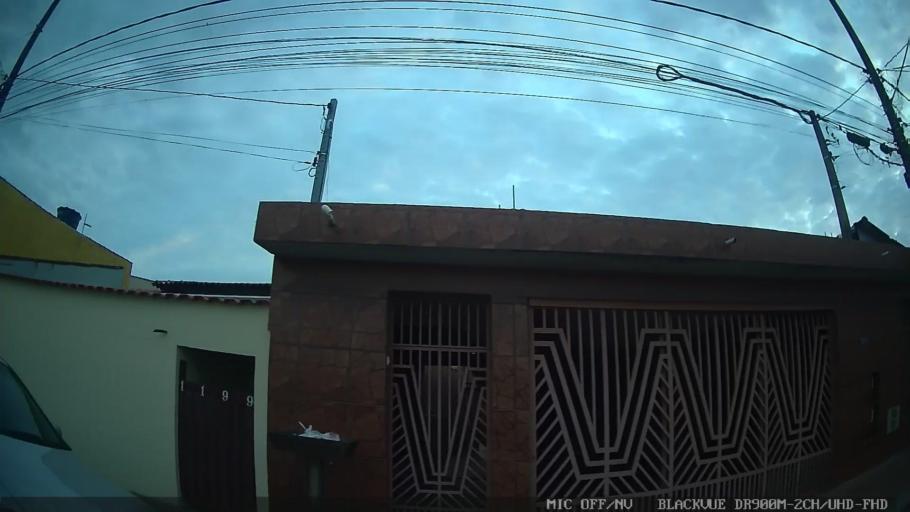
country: BR
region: Sao Paulo
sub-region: Itanhaem
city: Itanhaem
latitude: -24.1717
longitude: -46.7827
